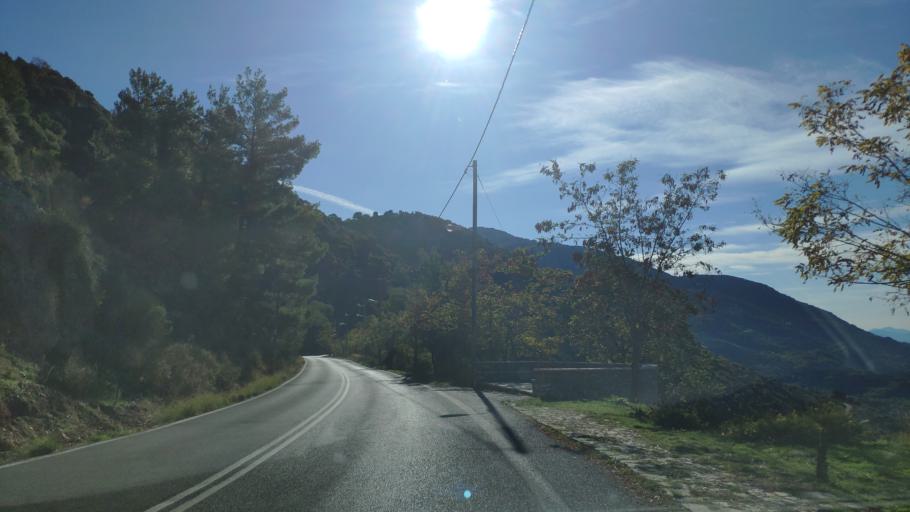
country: GR
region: Peloponnese
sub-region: Nomos Arkadias
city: Dimitsana
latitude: 37.5887
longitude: 22.0442
